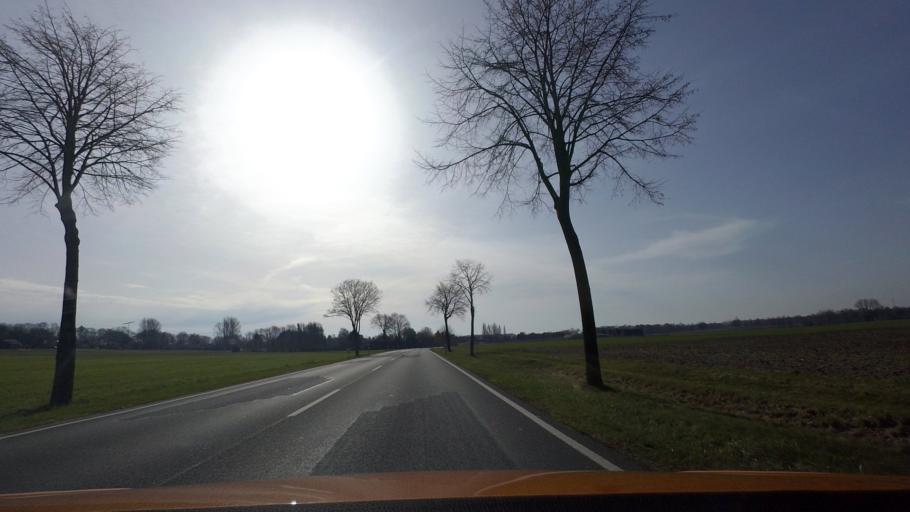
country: DE
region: Lower Saxony
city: Uchte
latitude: 52.5108
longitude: 8.9029
